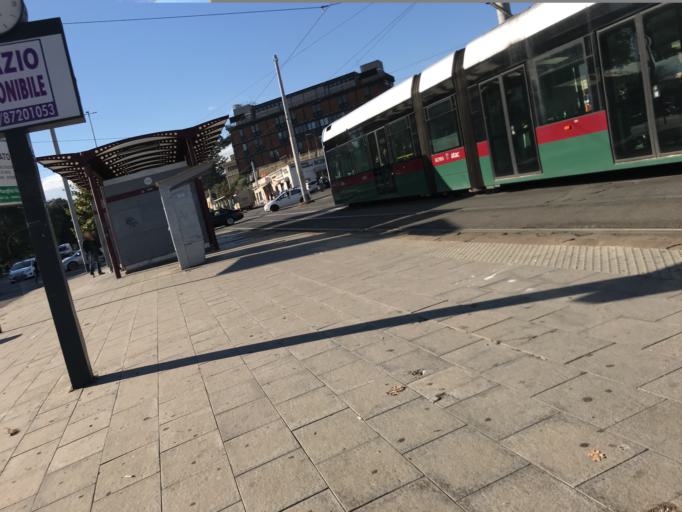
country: IT
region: Latium
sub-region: Citta metropolitana di Roma Capitale
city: Rome
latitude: 41.9024
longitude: 12.5191
